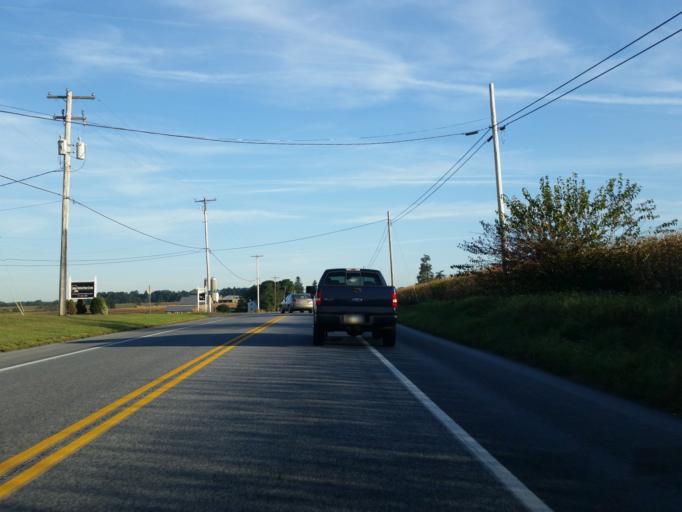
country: US
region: Pennsylvania
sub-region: Lancaster County
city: Quarryville
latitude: 39.8449
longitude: -76.2194
